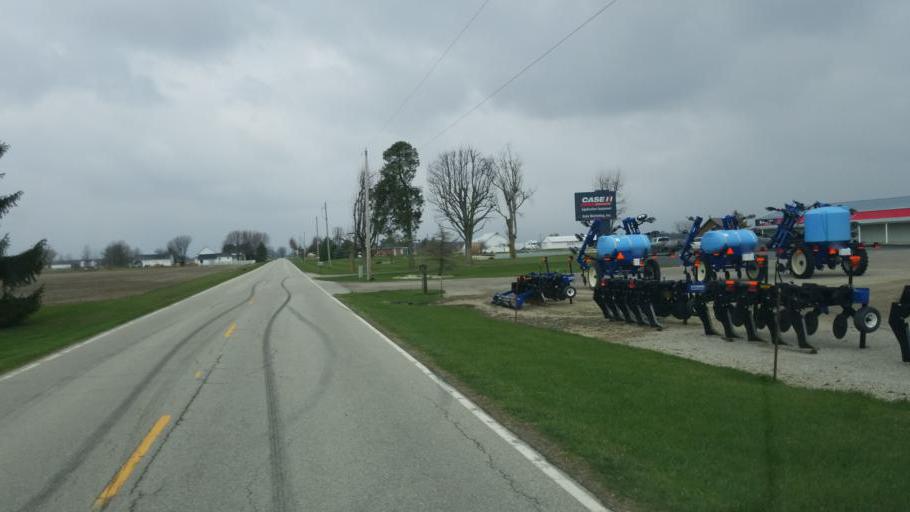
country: US
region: Ohio
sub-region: Union County
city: Richwood
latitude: 40.4256
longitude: -83.3440
